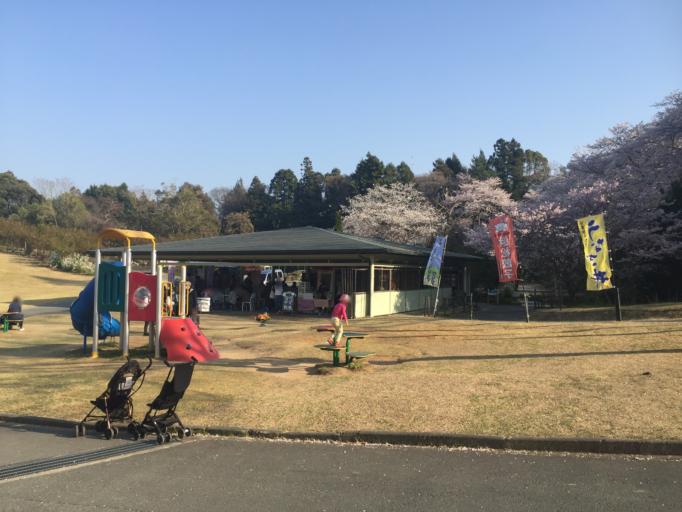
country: JP
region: Shizuoka
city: Kosai-shi
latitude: 34.7632
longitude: 137.6354
